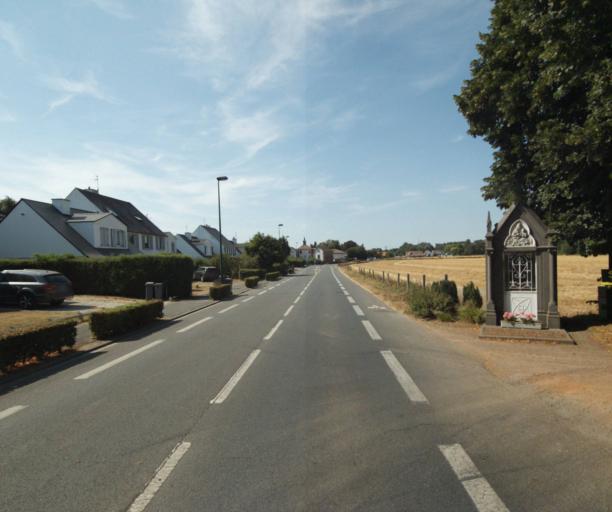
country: FR
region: Nord-Pas-de-Calais
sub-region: Departement du Nord
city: Bondues
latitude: 50.7071
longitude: 3.0902
